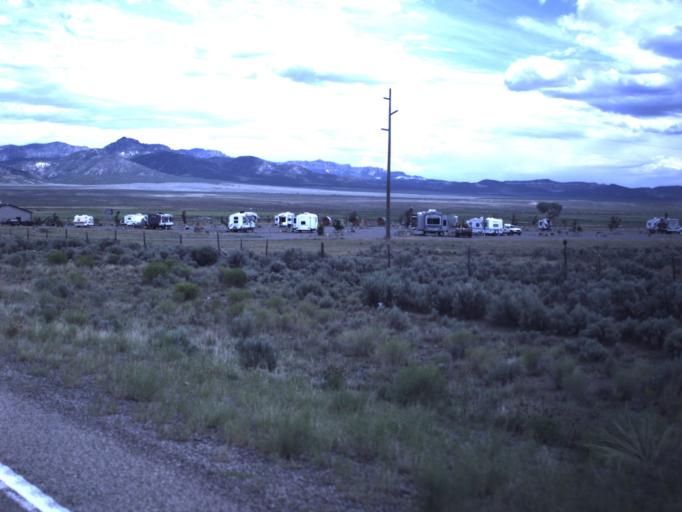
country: US
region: Utah
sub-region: Garfield County
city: Panguitch
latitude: 37.9659
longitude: -112.4206
